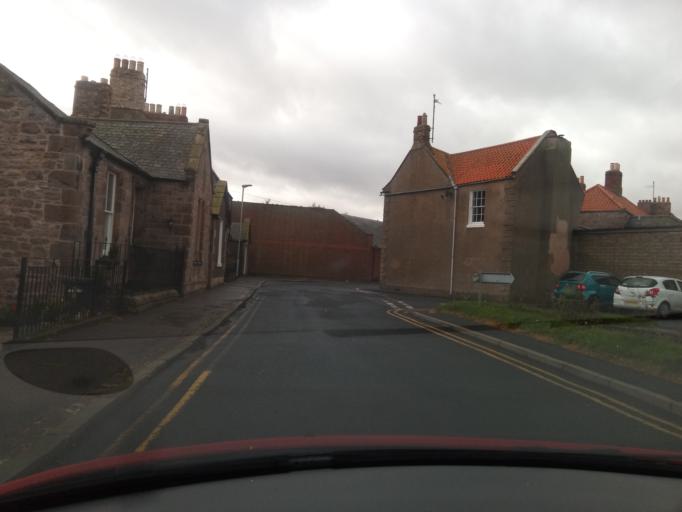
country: GB
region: England
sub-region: Northumberland
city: Berwick-Upon-Tweed
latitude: 55.7722
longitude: -2.0063
